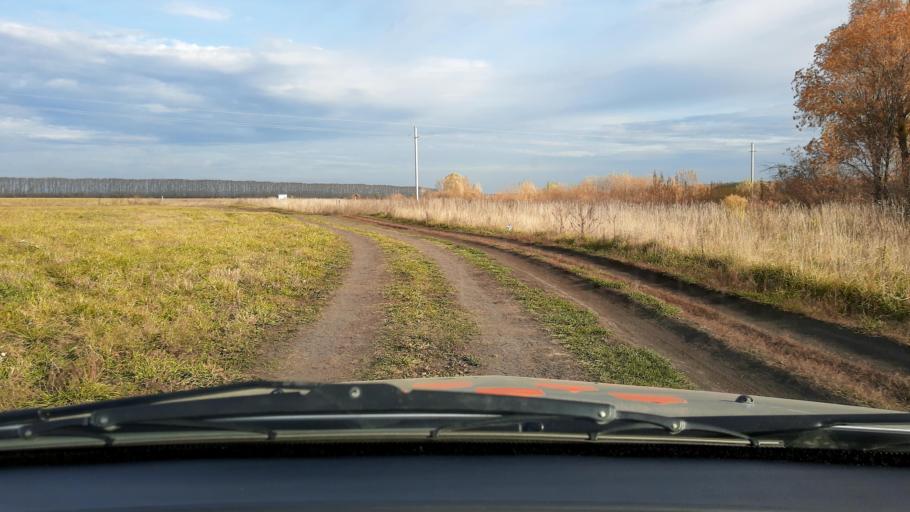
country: RU
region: Bashkortostan
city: Asanovo
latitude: 54.8082
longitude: 55.6116
